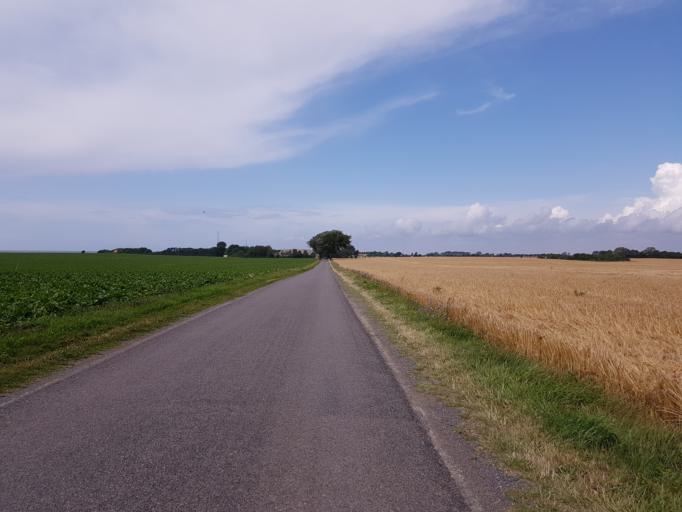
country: DK
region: Zealand
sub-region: Guldborgsund Kommune
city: Nykobing Falster
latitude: 54.5656
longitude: 11.9607
